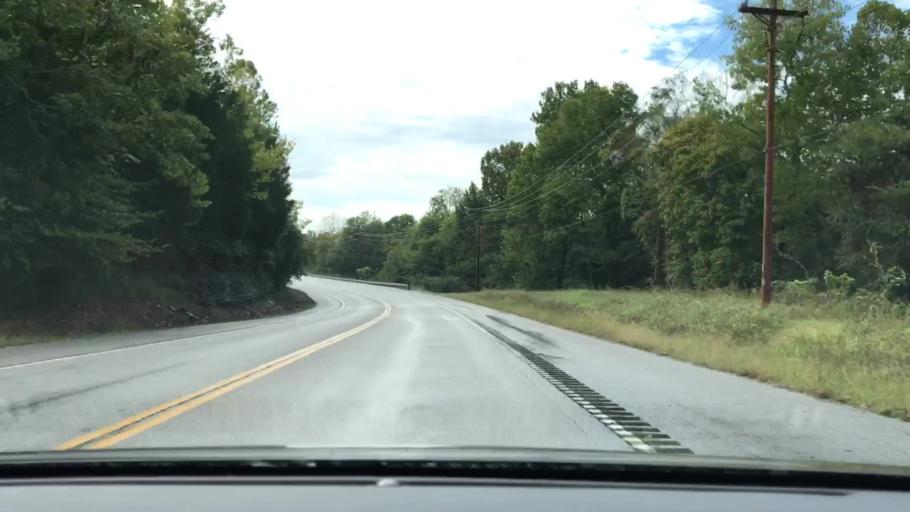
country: US
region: Tennessee
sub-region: Smith County
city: Carthage
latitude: 36.2908
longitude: -85.9869
